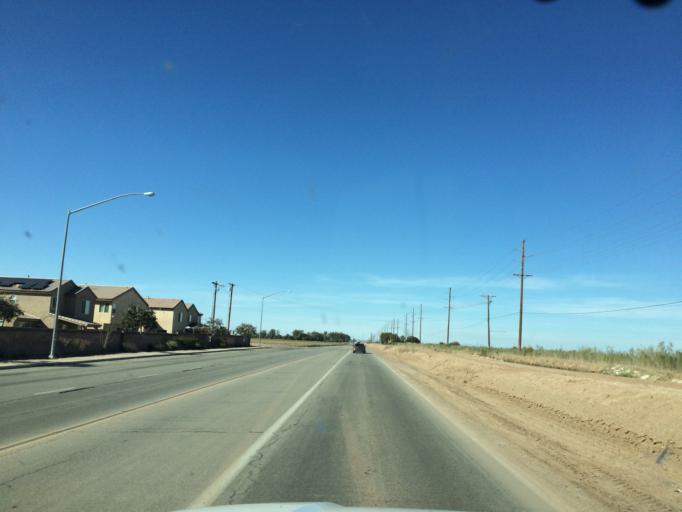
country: US
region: California
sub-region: Imperial County
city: Heber
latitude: 32.7404
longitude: -115.5346
